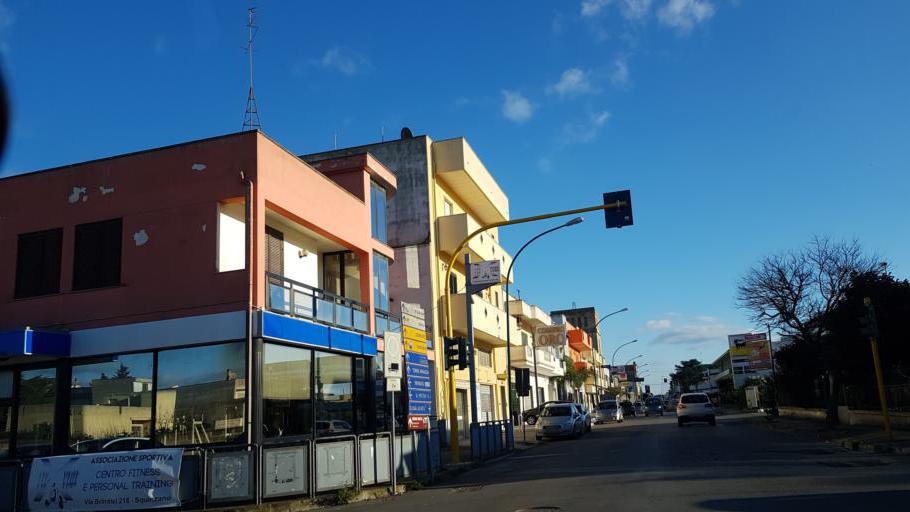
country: IT
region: Apulia
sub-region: Provincia di Lecce
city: Squinzano
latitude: 40.4415
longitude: 18.0356
